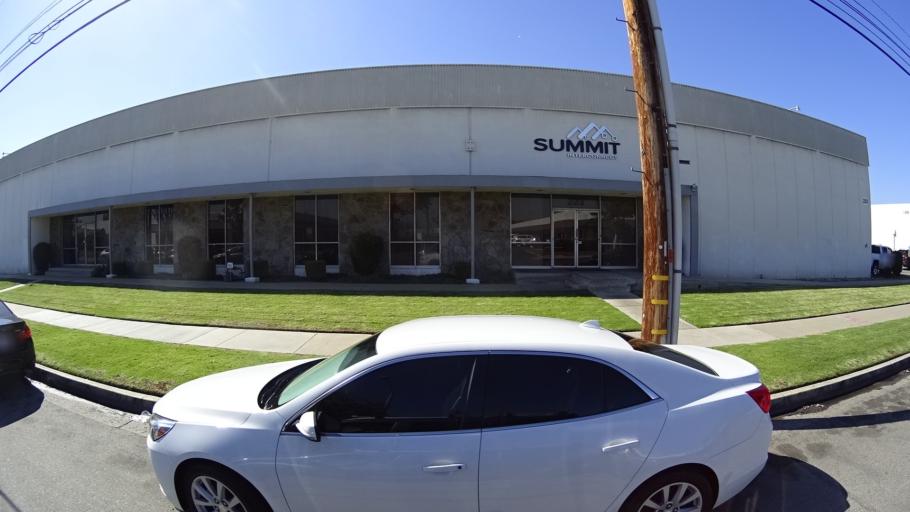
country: US
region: California
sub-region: Orange County
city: Anaheim
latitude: 33.8347
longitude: -117.9474
